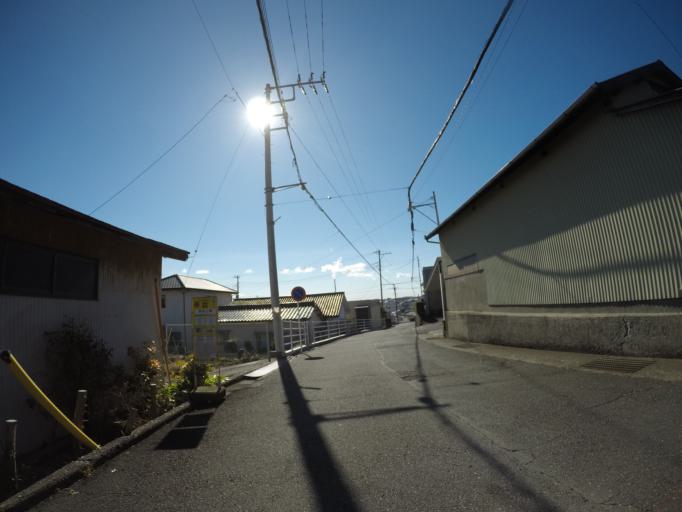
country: JP
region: Shizuoka
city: Fuji
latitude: 35.1681
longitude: 138.6924
